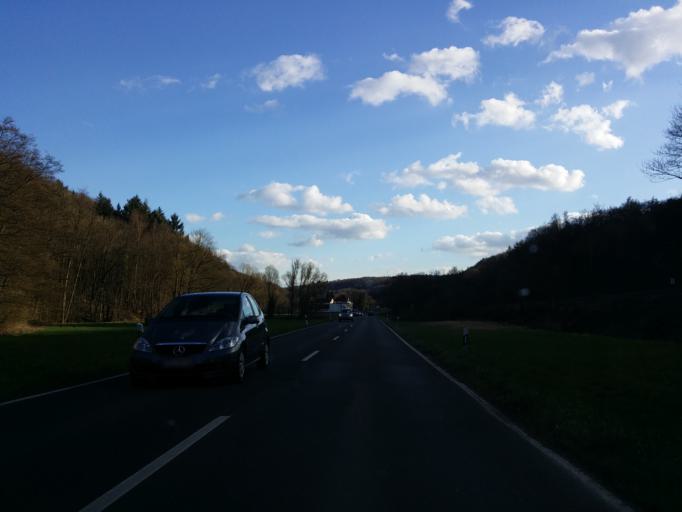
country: DE
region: Hesse
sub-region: Regierungsbezirk Darmstadt
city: Hofheim am Taunus
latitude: 50.1045
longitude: 8.4280
